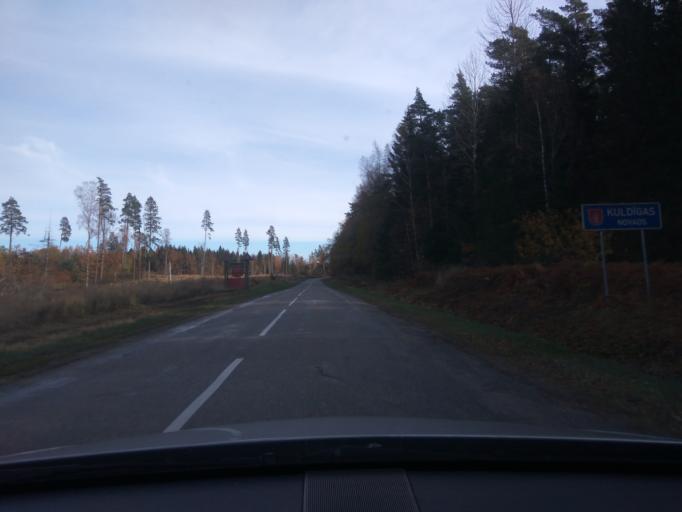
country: LV
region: Alsunga
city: Alsunga
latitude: 56.9981
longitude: 21.6476
